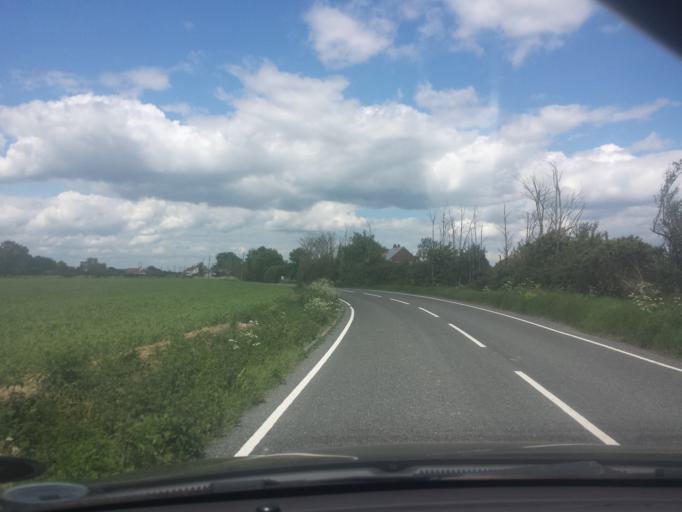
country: GB
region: England
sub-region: Essex
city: Little Clacton
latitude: 51.8364
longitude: 1.1556
